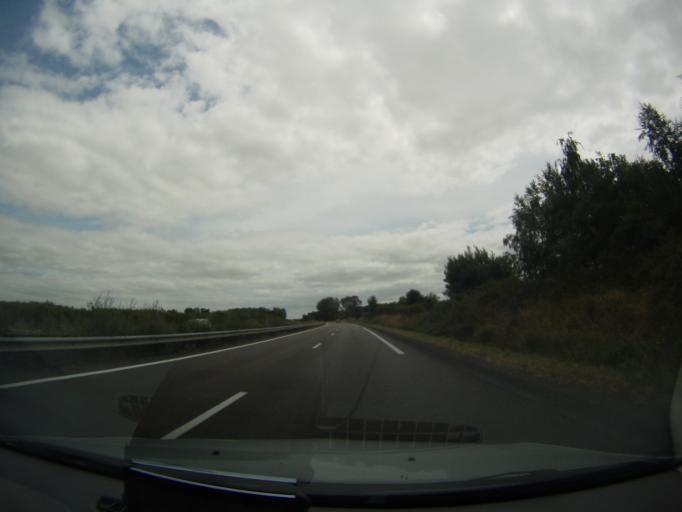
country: FR
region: Pays de la Loire
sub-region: Departement de la Loire-Atlantique
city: La Chapelle-Heulin
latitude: 47.1634
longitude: -1.3670
